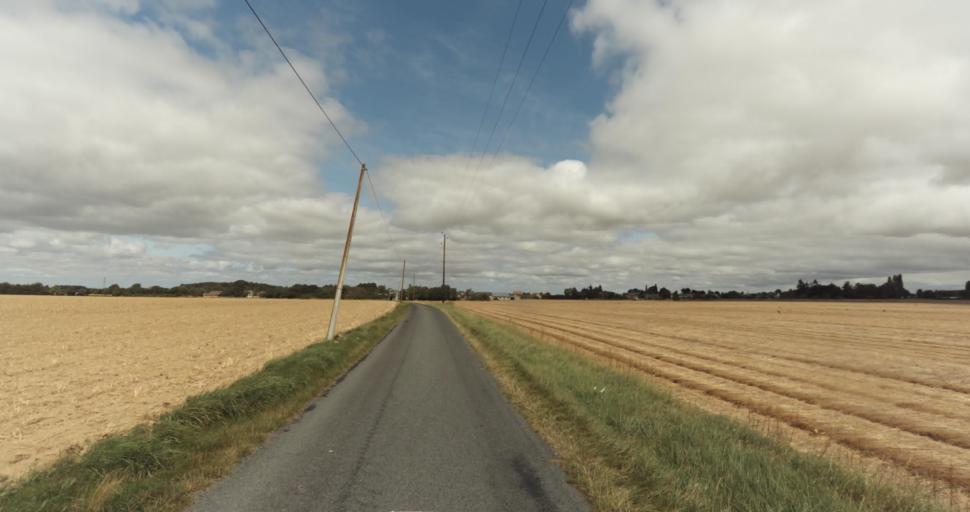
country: FR
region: Haute-Normandie
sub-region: Departement de l'Eure
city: Evreux
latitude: 48.9094
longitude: 1.2084
